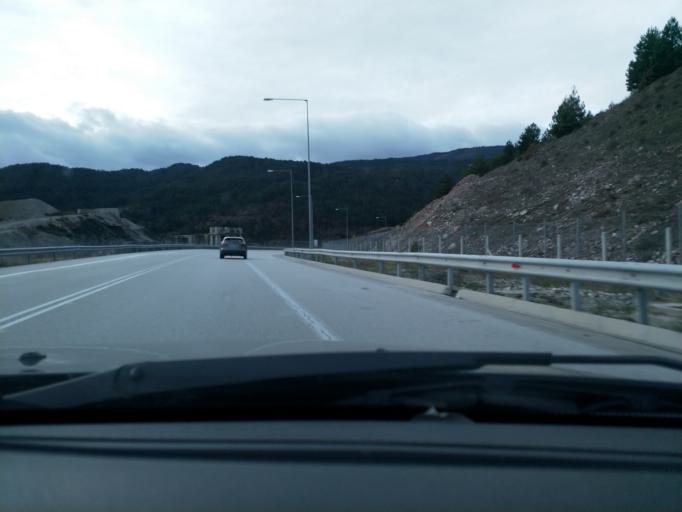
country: GR
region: Epirus
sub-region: Nomos Ioanninon
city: Metsovo
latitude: 39.7910
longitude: 21.3093
